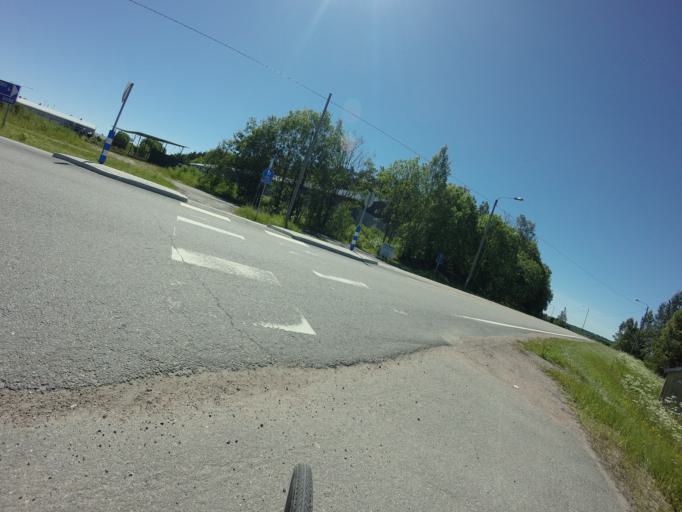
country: FI
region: Varsinais-Suomi
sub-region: Turku
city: Turku
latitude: 60.4933
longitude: 22.3341
